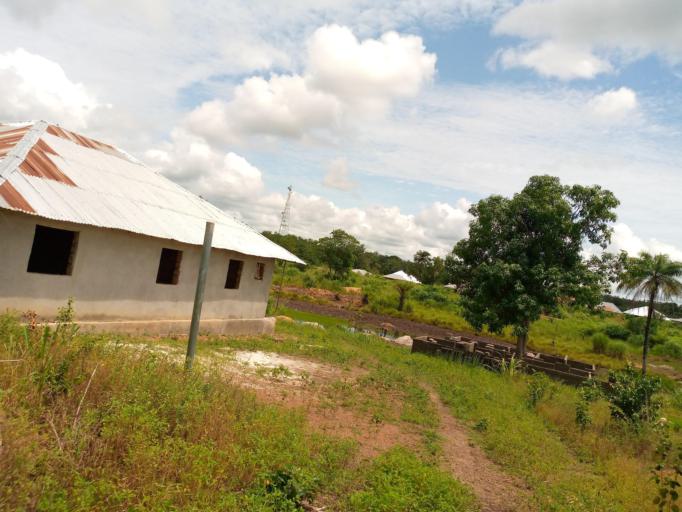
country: SL
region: Northern Province
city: Magburaka
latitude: 8.7192
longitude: -11.9269
